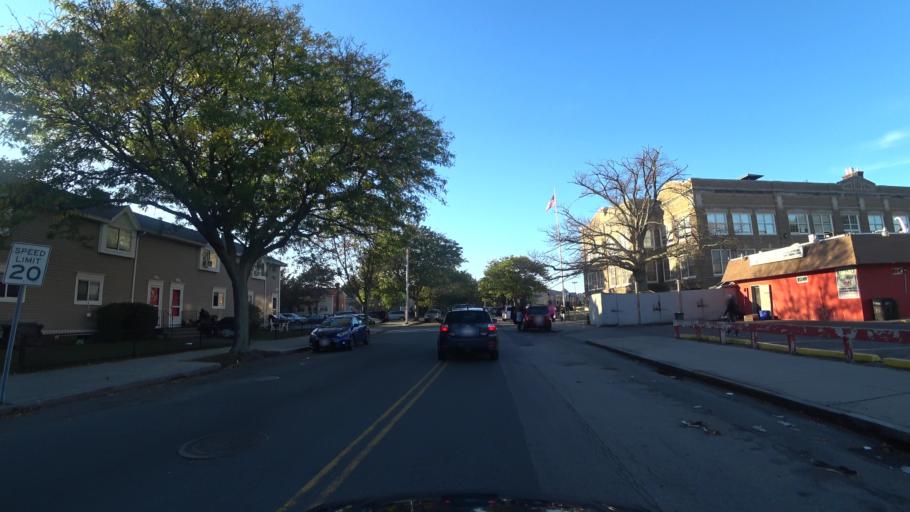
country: US
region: Massachusetts
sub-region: Essex County
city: Lynn
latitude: 42.4610
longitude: -70.9542
